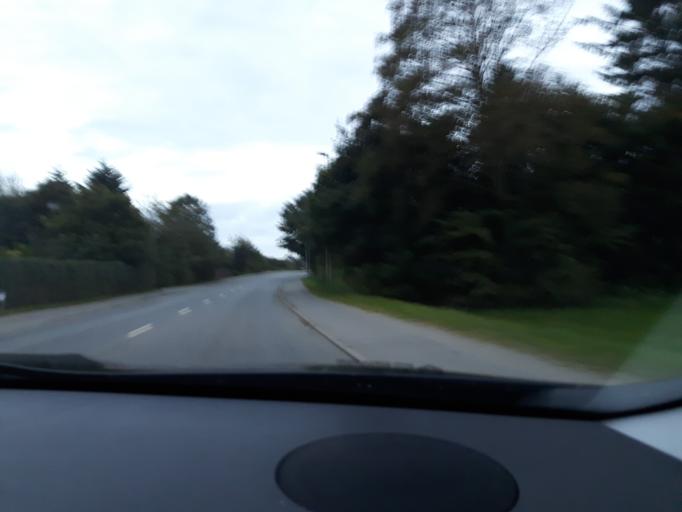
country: DK
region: North Denmark
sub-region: Hjorring Kommune
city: Hirtshals
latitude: 57.5275
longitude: 9.9495
